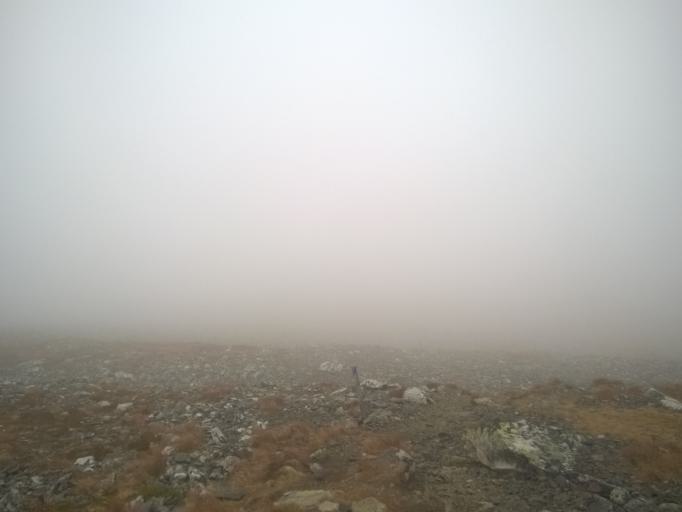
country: FI
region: Lapland
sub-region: Tunturi-Lappi
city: Muonio
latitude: 68.0760
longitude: 24.0588
